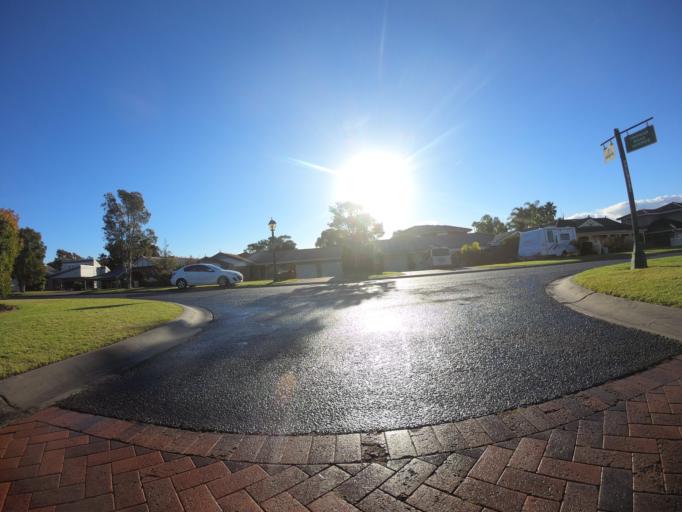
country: AU
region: New South Wales
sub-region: Wollongong
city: Bulli
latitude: -34.3569
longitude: 150.9150
